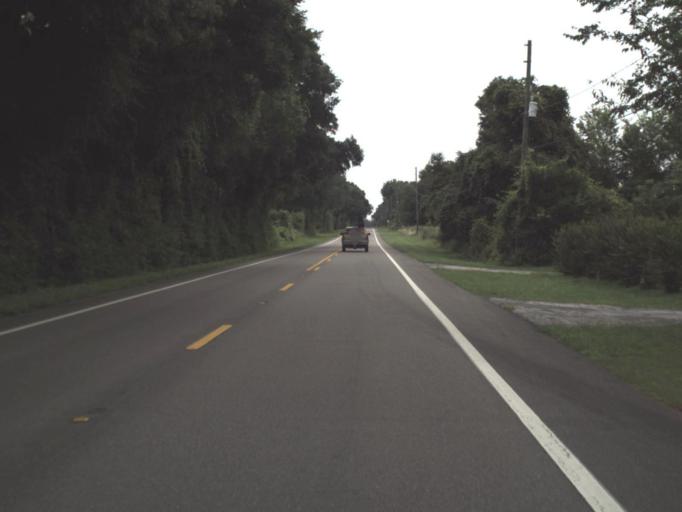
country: US
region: Florida
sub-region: Alachua County
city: Archer
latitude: 29.4939
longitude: -82.4946
